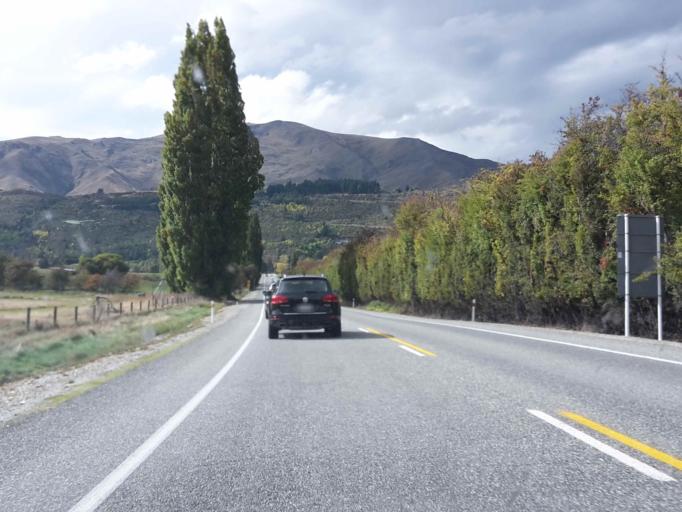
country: NZ
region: Otago
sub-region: Queenstown-Lakes District
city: Arrowtown
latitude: -44.9819
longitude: 168.8383
